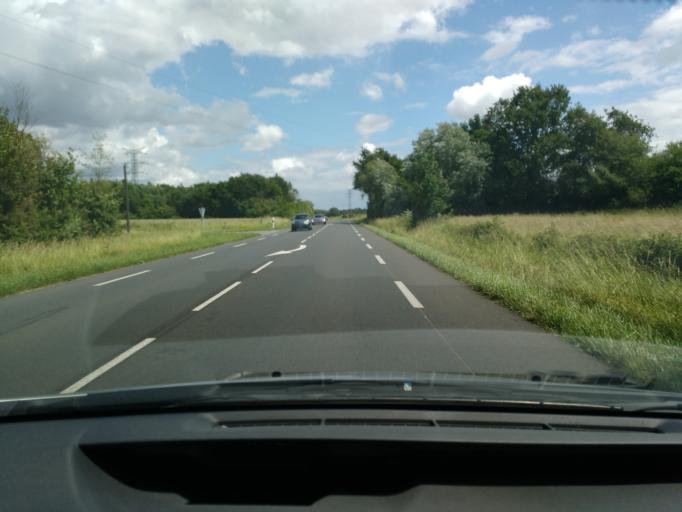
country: FR
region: Pays de la Loire
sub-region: Departement de Maine-et-Loire
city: Trelaze
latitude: 47.4870
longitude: -0.4743
